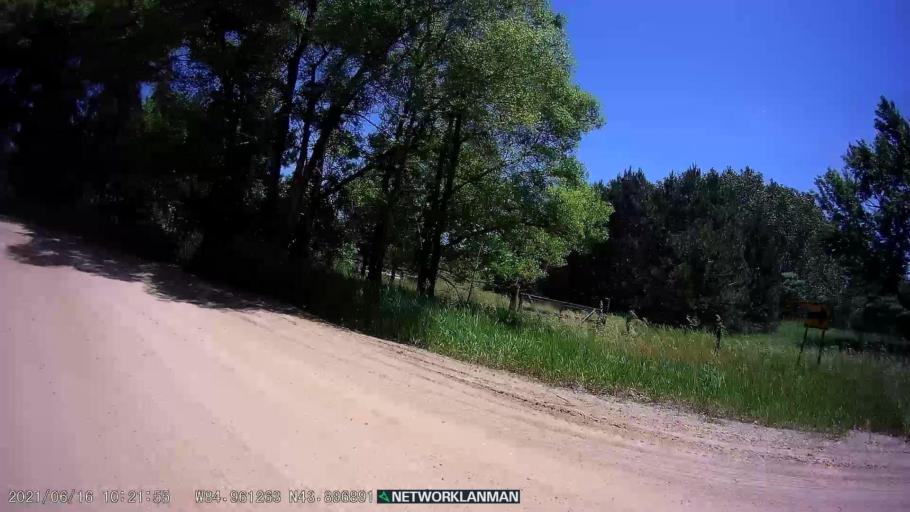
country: US
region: Michigan
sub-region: Clare County
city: Harrison
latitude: 43.8969
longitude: -84.9612
